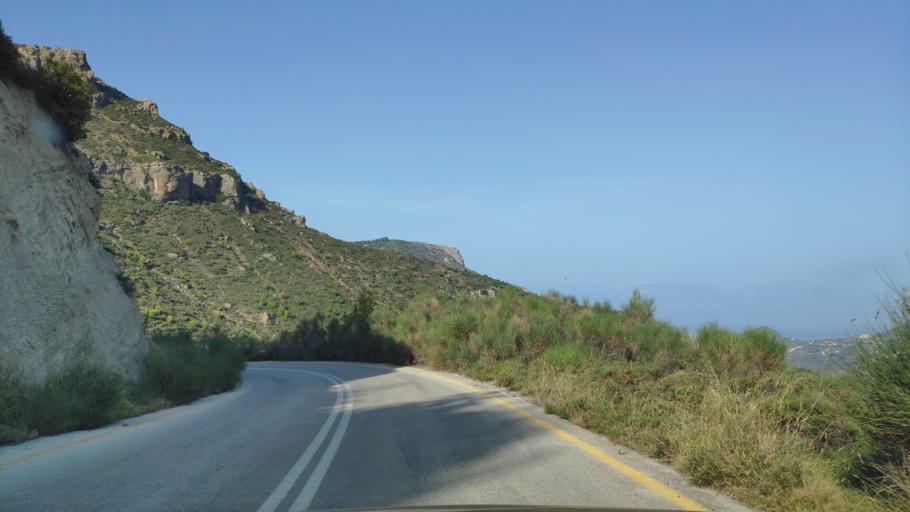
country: GR
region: West Greece
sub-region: Nomos Achaias
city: Aiyira
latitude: 38.0655
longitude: 22.3795
